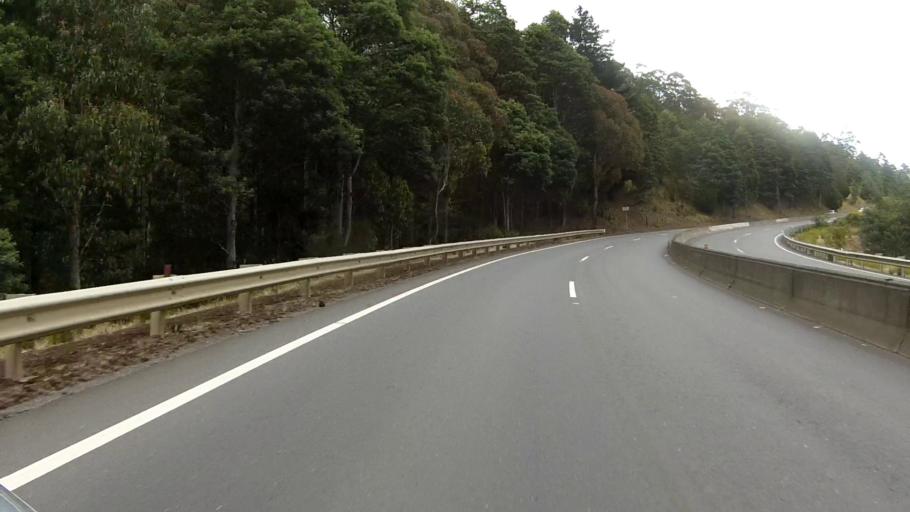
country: AU
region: Tasmania
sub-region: Kingborough
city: Margate
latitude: -42.9816
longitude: 147.1738
